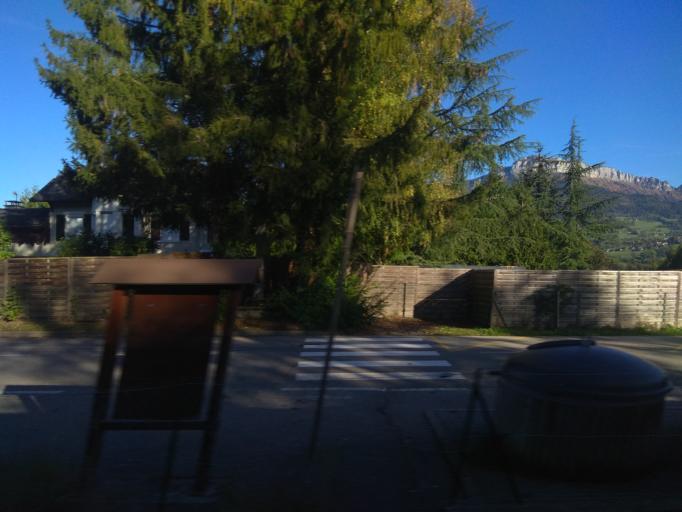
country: FR
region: Rhone-Alpes
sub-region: Departement de la Haute-Savoie
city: Saint-Martin-Bellevue
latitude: 45.9667
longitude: 6.1577
